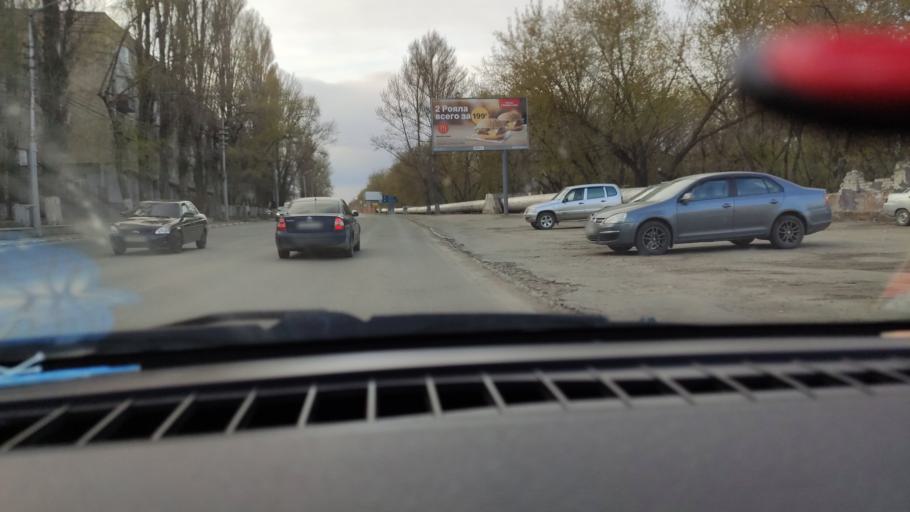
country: RU
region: Saratov
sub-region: Saratovskiy Rayon
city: Saratov
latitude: 51.5559
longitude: 46.0069
